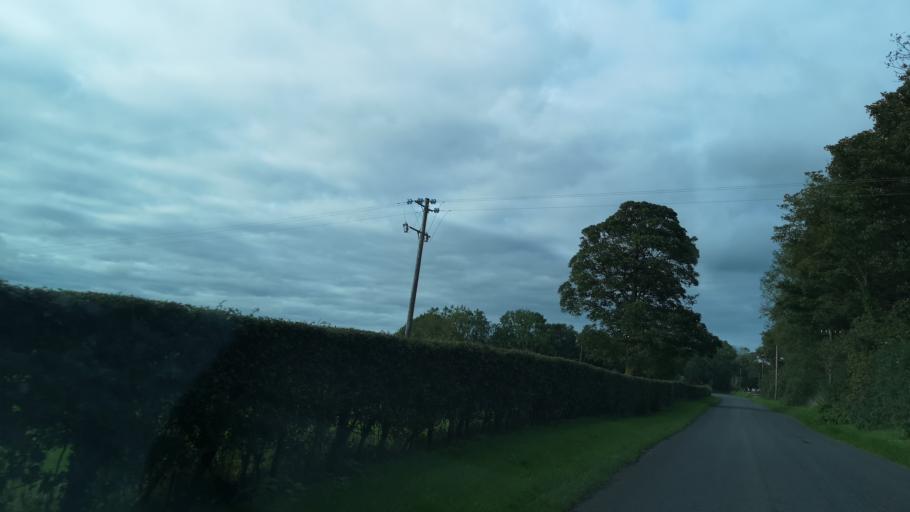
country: IE
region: Connaught
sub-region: County Galway
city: Ballinasloe
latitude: 53.3227
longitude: -8.1028
